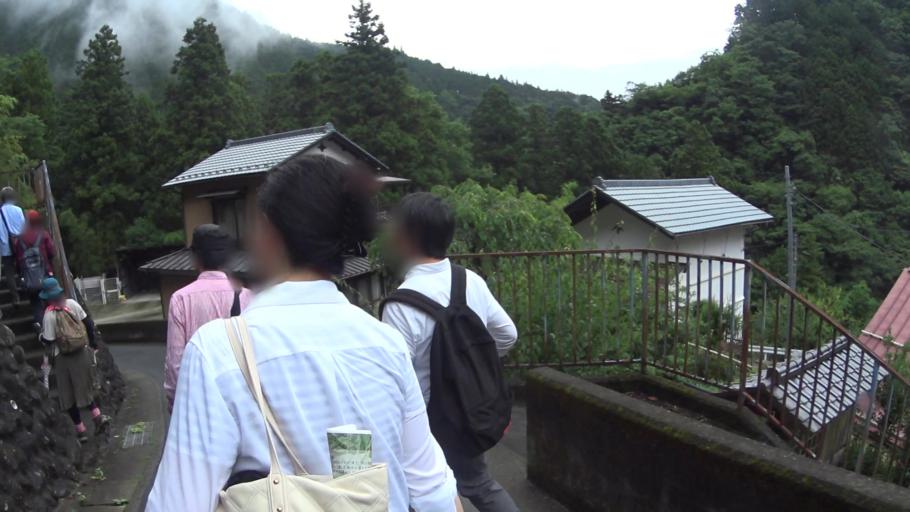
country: JP
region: Tokyo
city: Itsukaichi
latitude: 35.7998
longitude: 139.0777
